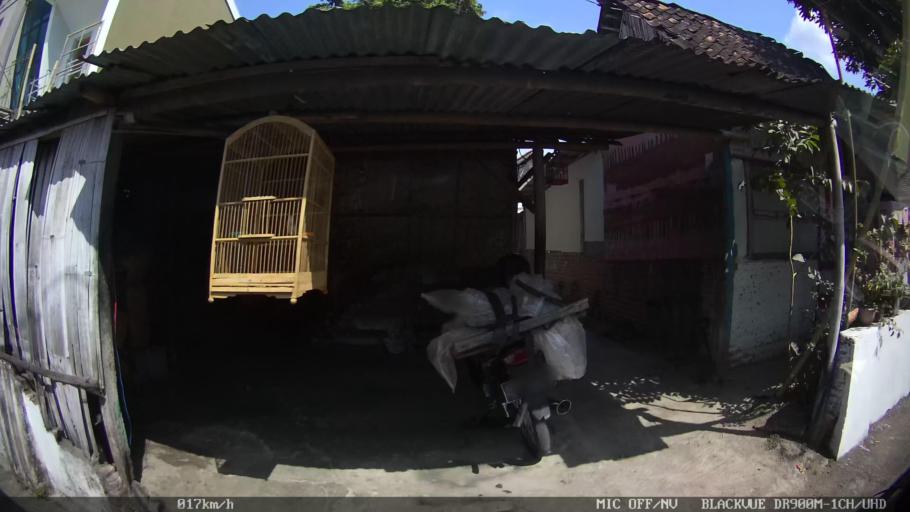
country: ID
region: Daerah Istimewa Yogyakarta
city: Kasihan
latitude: -7.8293
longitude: 110.3725
